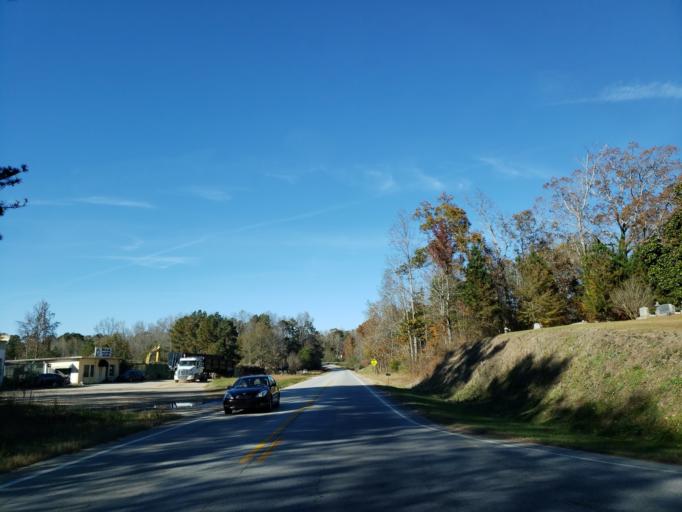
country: US
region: Alabama
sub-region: Calhoun County
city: Choccolocco
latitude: 33.5678
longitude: -85.6654
